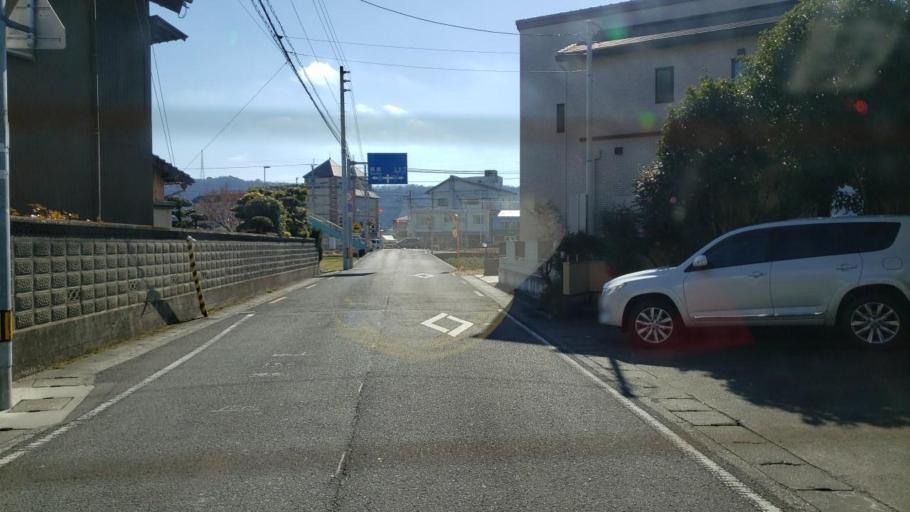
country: JP
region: Tokushima
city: Ishii
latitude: 34.0682
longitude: 134.4372
